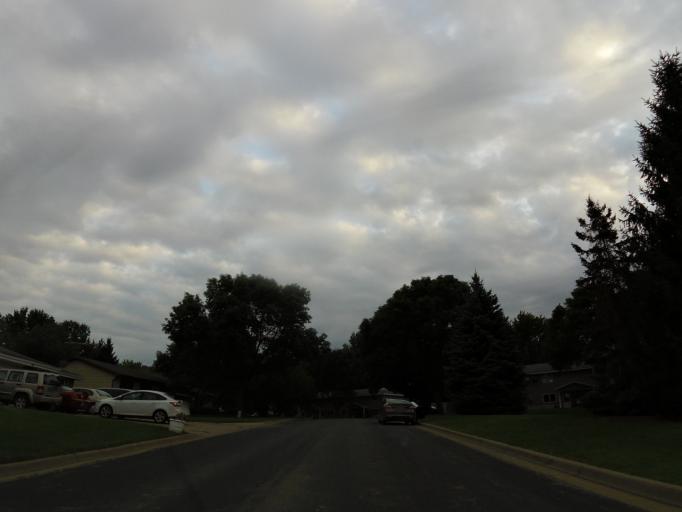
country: US
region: Minnesota
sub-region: Scott County
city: Prior Lake
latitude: 44.7074
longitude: -93.4231
